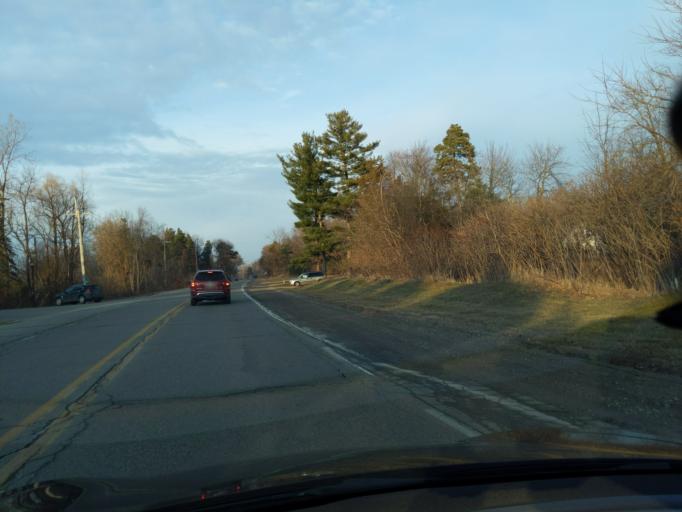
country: US
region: Michigan
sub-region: Livingston County
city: Brighton
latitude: 42.5622
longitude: -83.7549
